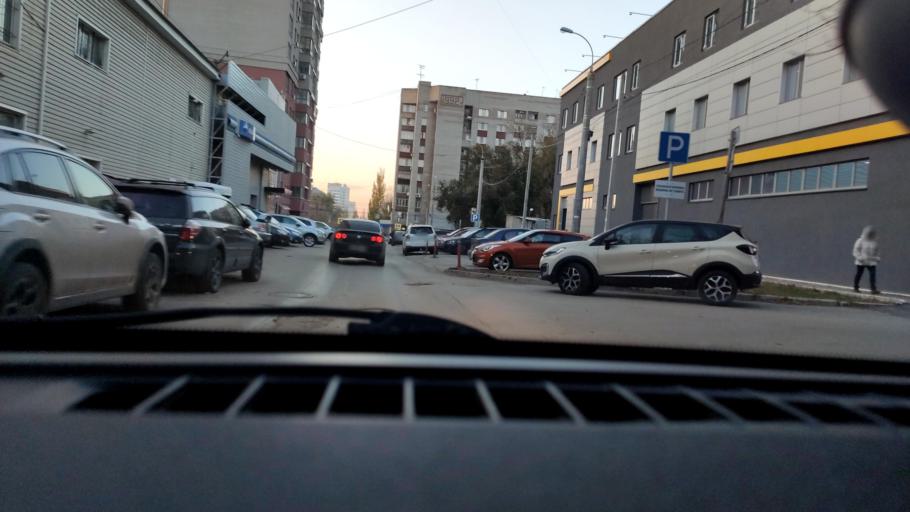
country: RU
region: Samara
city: Samara
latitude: 53.2074
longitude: 50.1809
